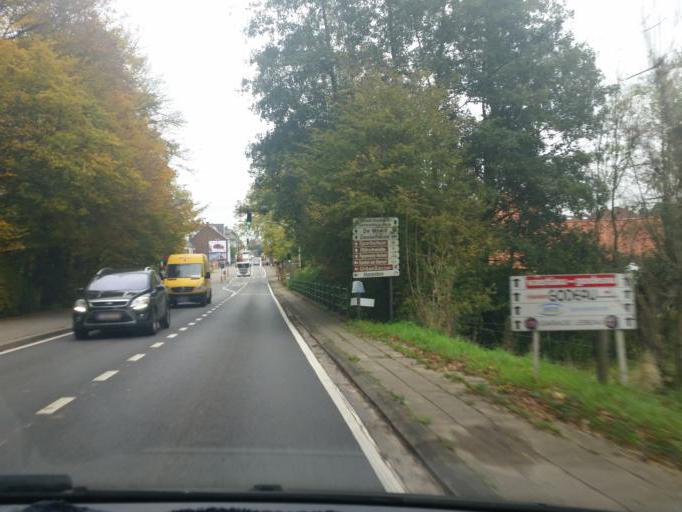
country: BE
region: Flanders
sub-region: Provincie Vlaams-Brabant
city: Beersel
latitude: 50.7319
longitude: 4.2938
